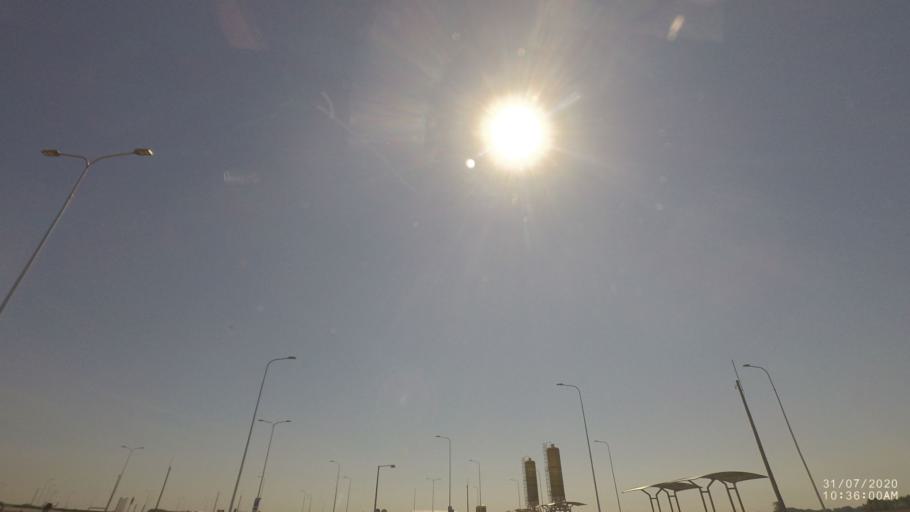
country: SK
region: Trnavsky
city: Samorin
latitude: 48.0113
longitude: 17.4560
